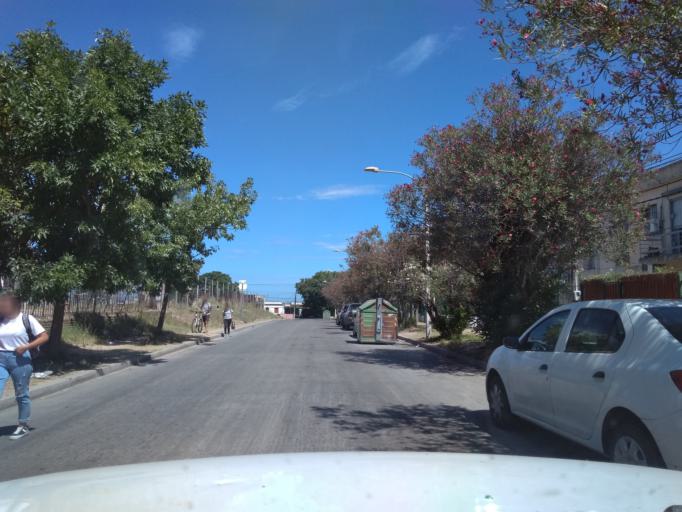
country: UY
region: Montevideo
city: Montevideo
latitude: -34.8878
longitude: -56.1213
